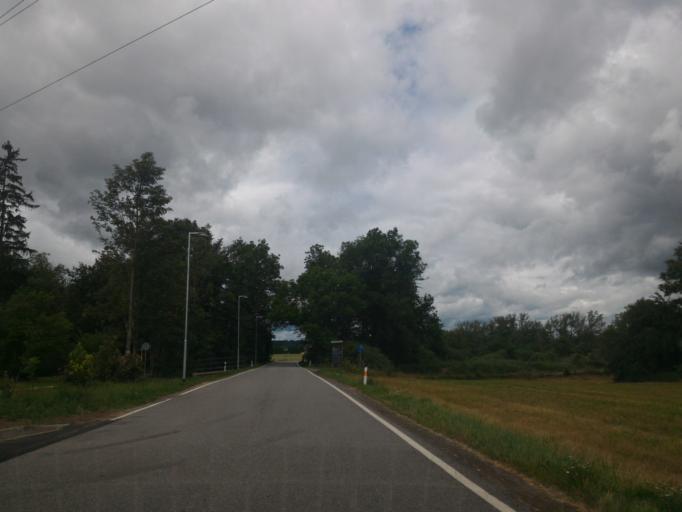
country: CZ
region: Vysocina
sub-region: Okres Jihlava
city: Telc
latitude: 49.1920
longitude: 15.4469
